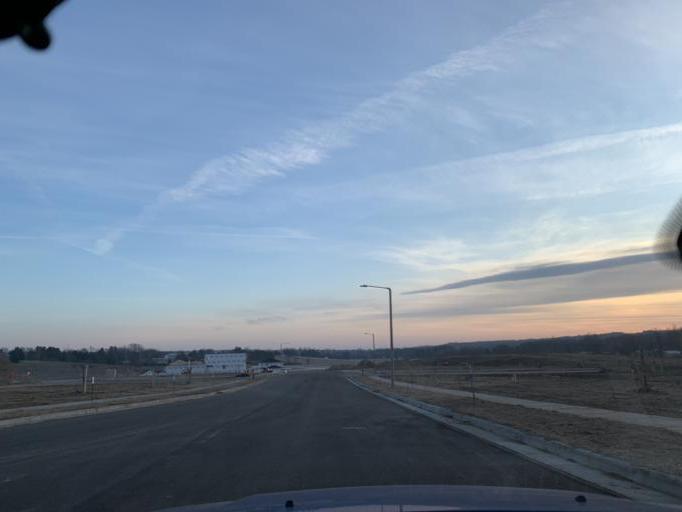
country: US
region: Wisconsin
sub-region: Dane County
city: Verona
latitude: 43.0512
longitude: -89.5650
